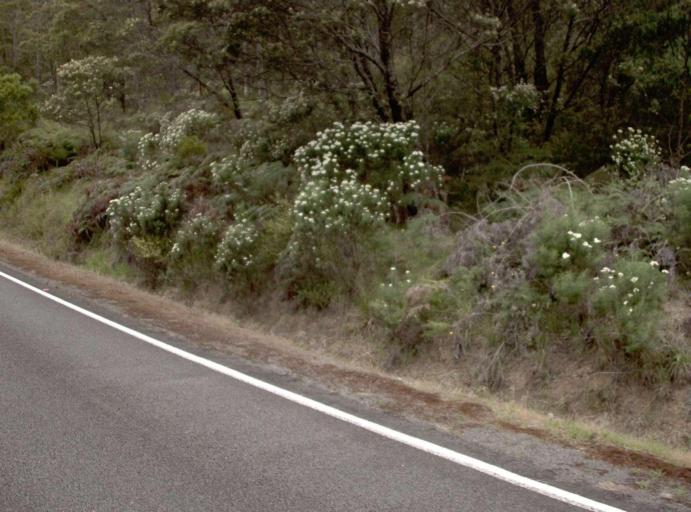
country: AU
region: New South Wales
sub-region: Bombala
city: Bombala
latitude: -37.2331
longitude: 149.2711
